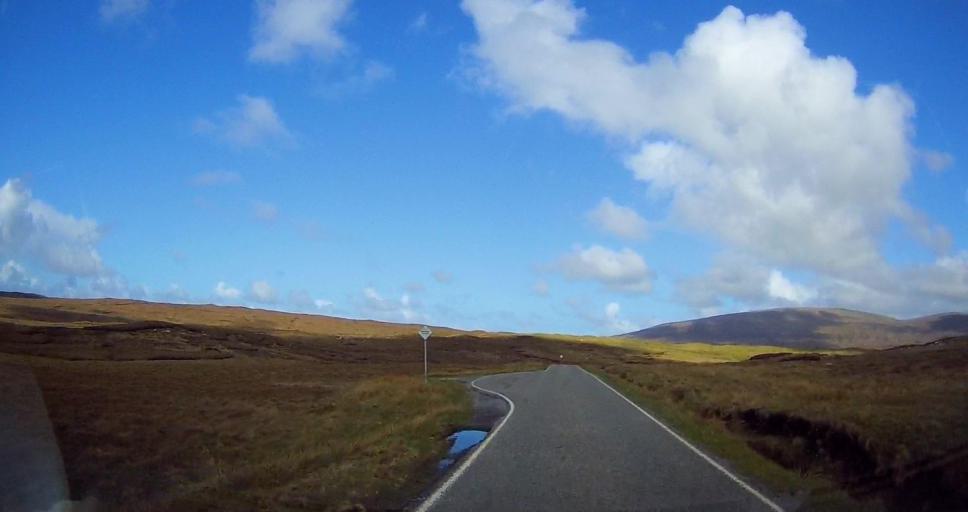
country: GB
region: Scotland
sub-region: Shetland Islands
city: Lerwick
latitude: 60.4958
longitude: -1.3932
